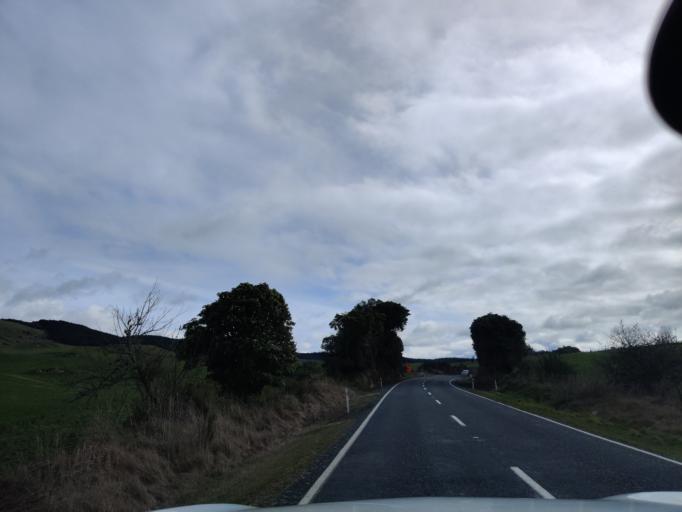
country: NZ
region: Waikato
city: Turangi
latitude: -38.7820
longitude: 175.6763
